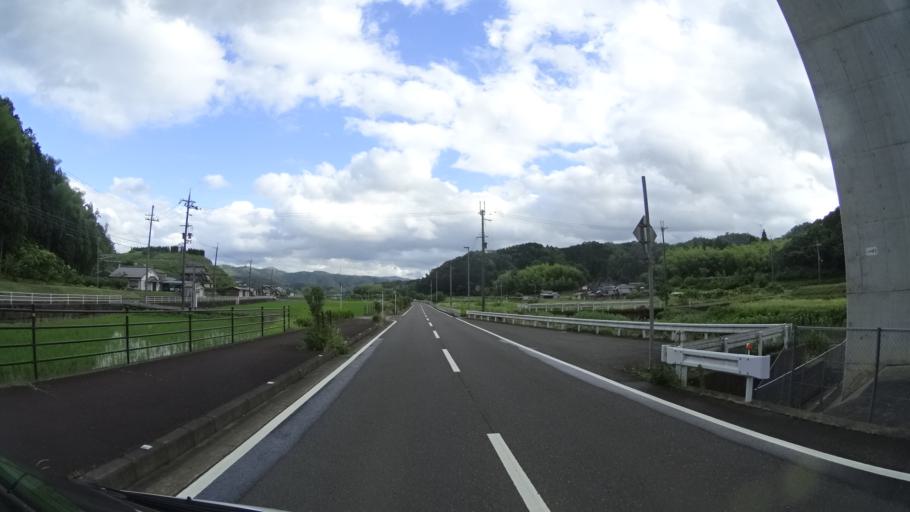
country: JP
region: Kyoto
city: Ayabe
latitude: 35.3475
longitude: 135.2883
